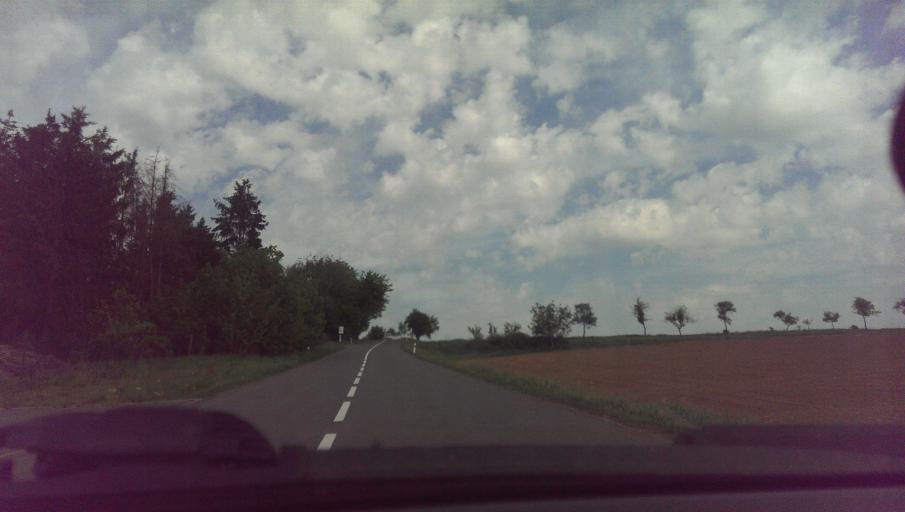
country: CZ
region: Zlin
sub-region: Okres Zlin
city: Otrokovice
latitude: 49.2479
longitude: 17.5436
